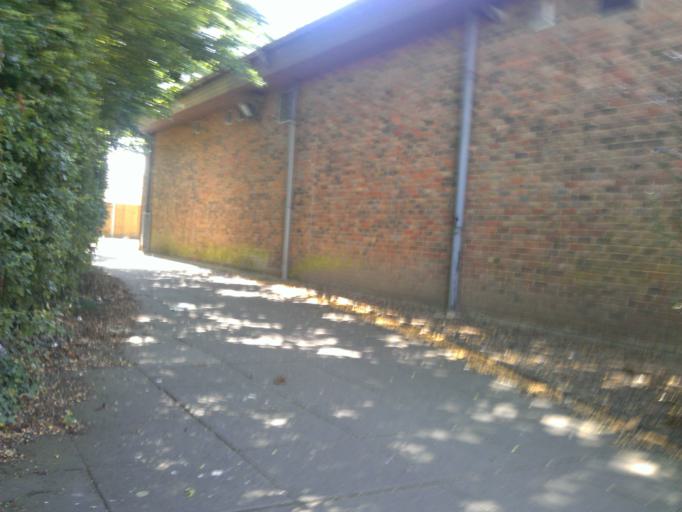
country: GB
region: England
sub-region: Essex
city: Clacton-on-Sea
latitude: 51.8055
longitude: 1.1560
